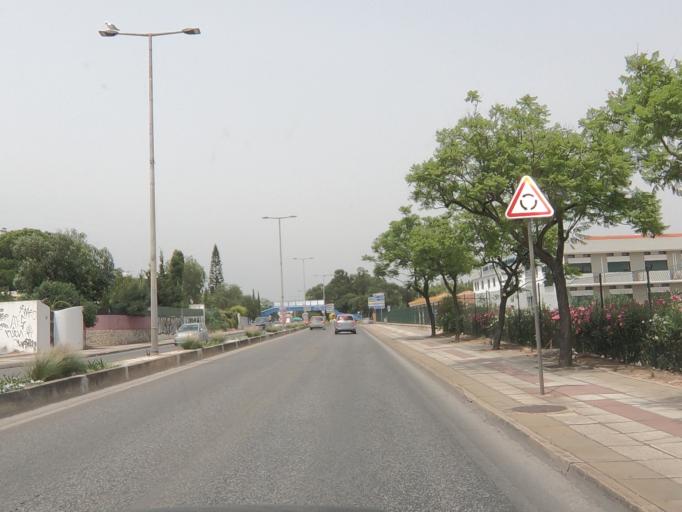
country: PT
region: Faro
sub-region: Portimao
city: Portimao
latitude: 37.1379
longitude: -8.5460
